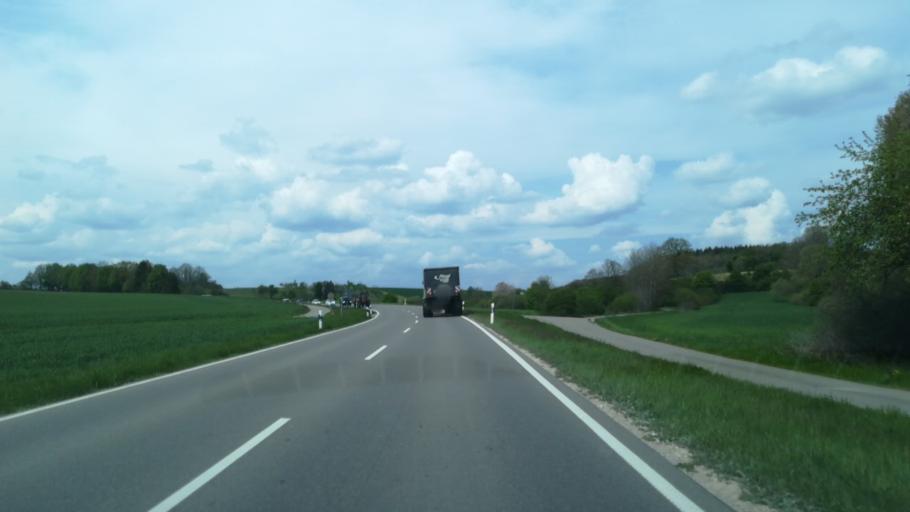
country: DE
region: Baden-Wuerttemberg
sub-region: Tuebingen Region
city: Messkirch
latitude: 48.0082
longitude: 9.1149
